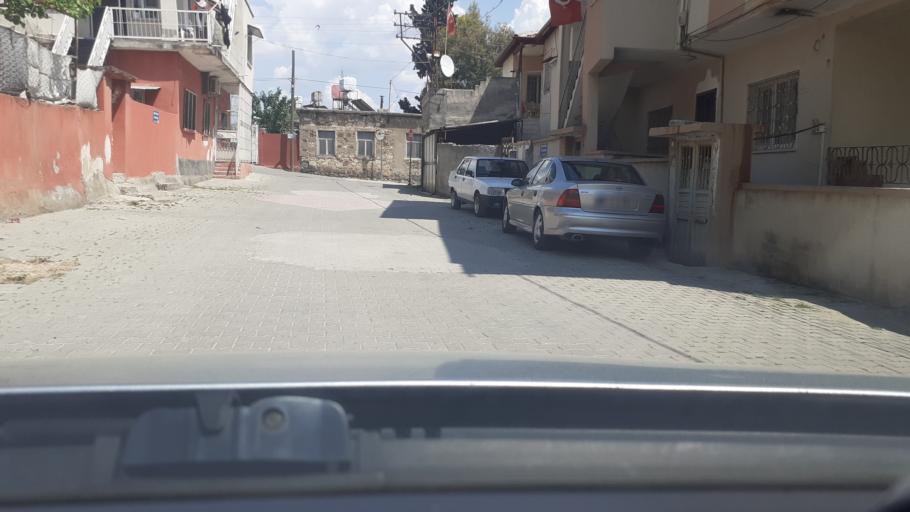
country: TR
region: Hatay
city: Kirikhan
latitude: 36.5020
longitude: 36.3588
